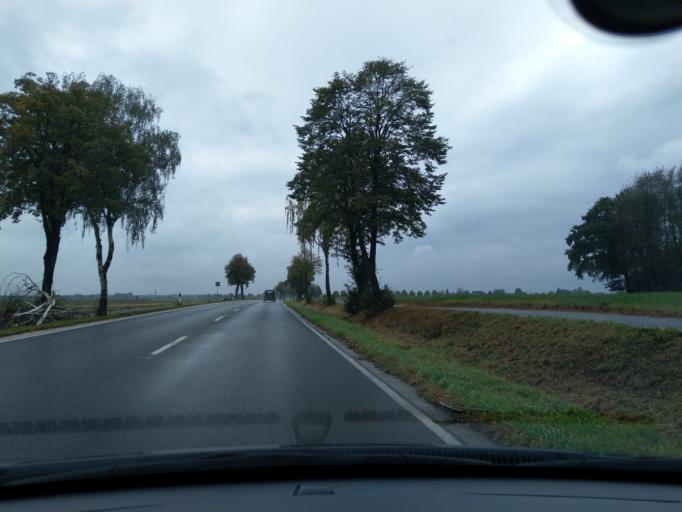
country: DE
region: North Rhine-Westphalia
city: Wegberg
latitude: 51.1147
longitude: 6.2941
